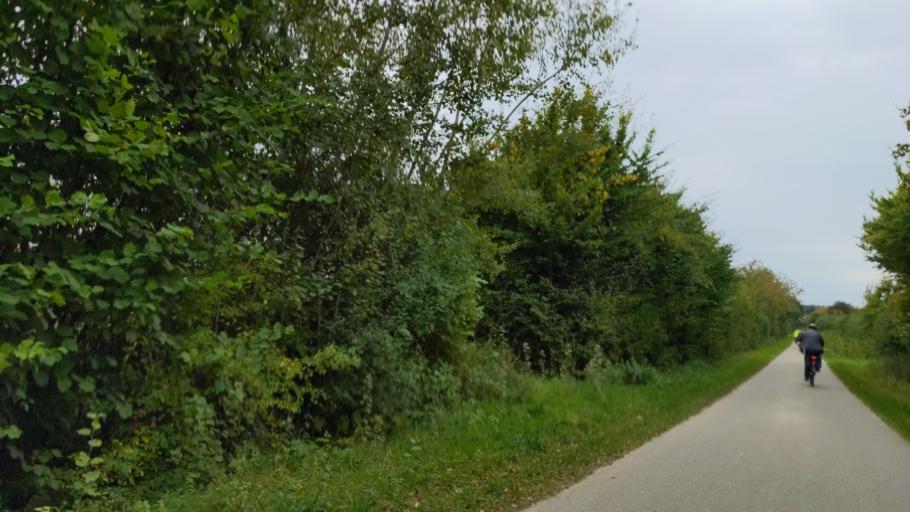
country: DE
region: Schleswig-Holstein
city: Bak
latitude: 53.7200
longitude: 10.7842
